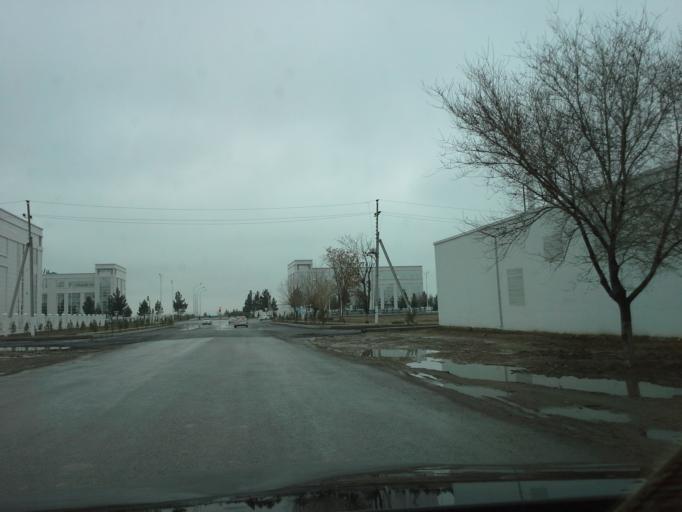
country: TM
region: Ahal
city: Ashgabat
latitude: 37.9537
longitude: 58.4265
